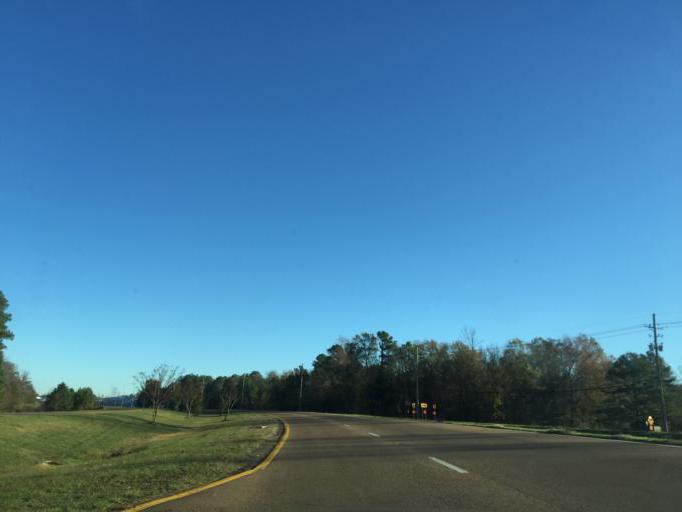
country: US
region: Mississippi
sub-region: Rankin County
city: Flowood
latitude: 32.2935
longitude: -90.1460
